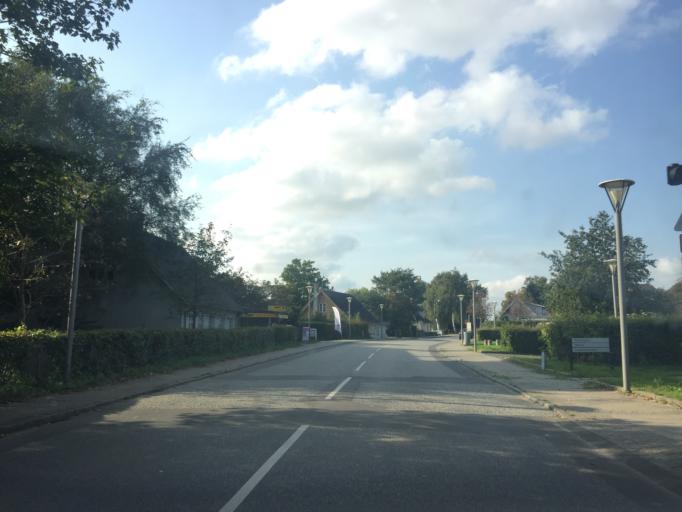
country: DK
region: Zealand
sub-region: Kalundborg Kommune
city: Gorlev
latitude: 55.6200
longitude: 11.2096
